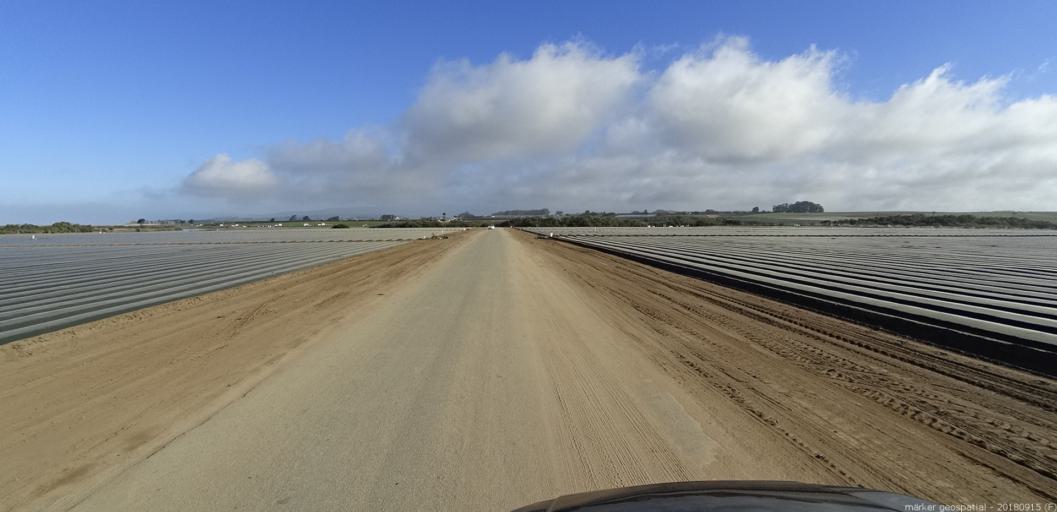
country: US
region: California
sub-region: Monterey County
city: Elkhorn
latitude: 36.8357
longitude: -121.7952
